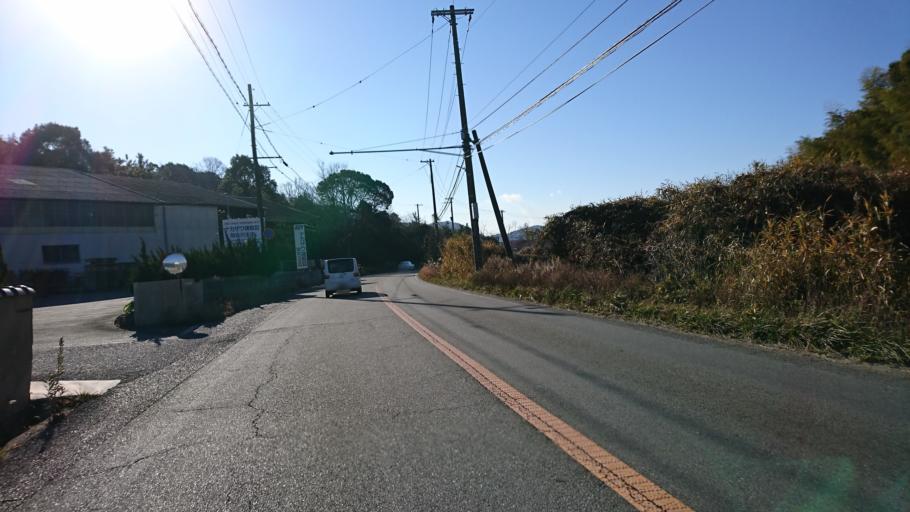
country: JP
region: Hyogo
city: Kakogawacho-honmachi
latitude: 34.8204
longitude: 134.8355
